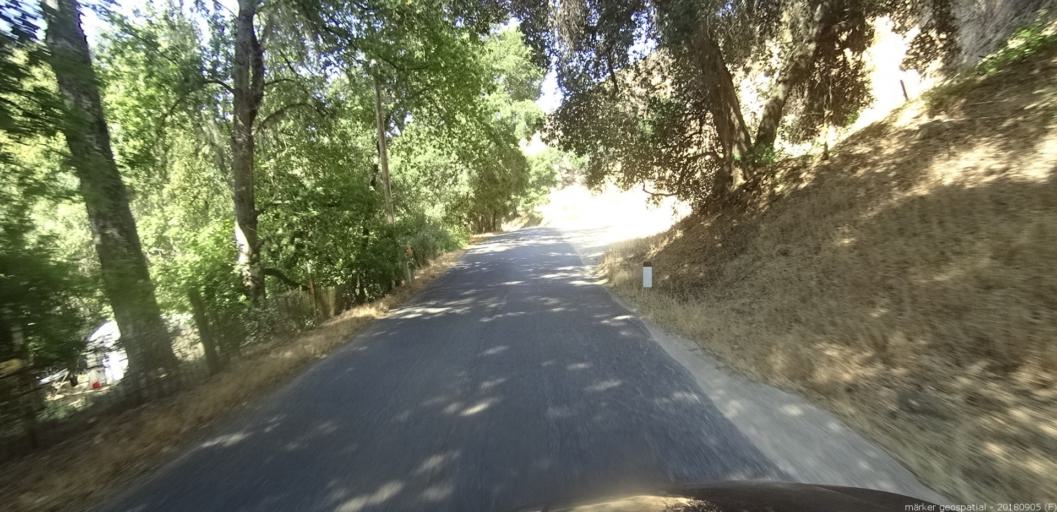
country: US
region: California
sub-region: Monterey County
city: Gonzales
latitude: 36.3941
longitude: -121.5842
